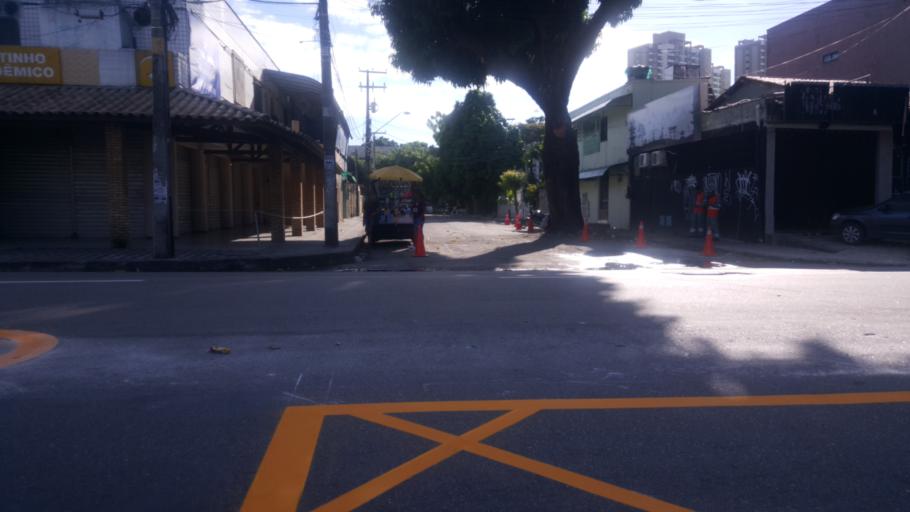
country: BR
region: Ceara
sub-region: Fortaleza
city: Fortaleza
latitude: -3.7422
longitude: -38.5372
